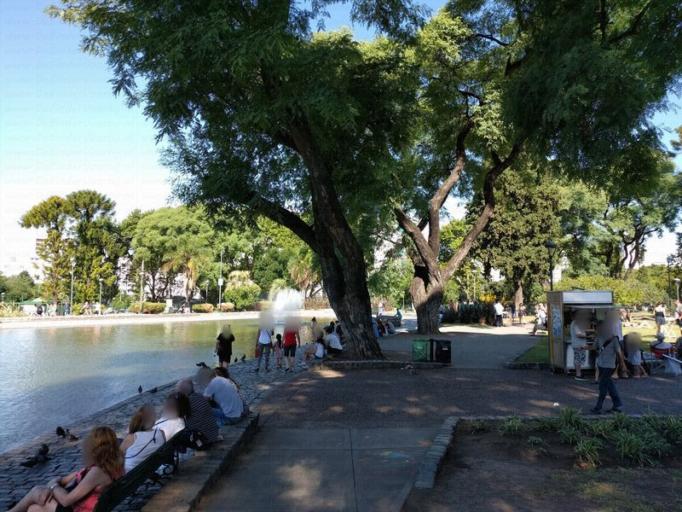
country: AR
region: Buenos Aires F.D.
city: Colegiales
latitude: -34.6070
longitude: -58.4352
